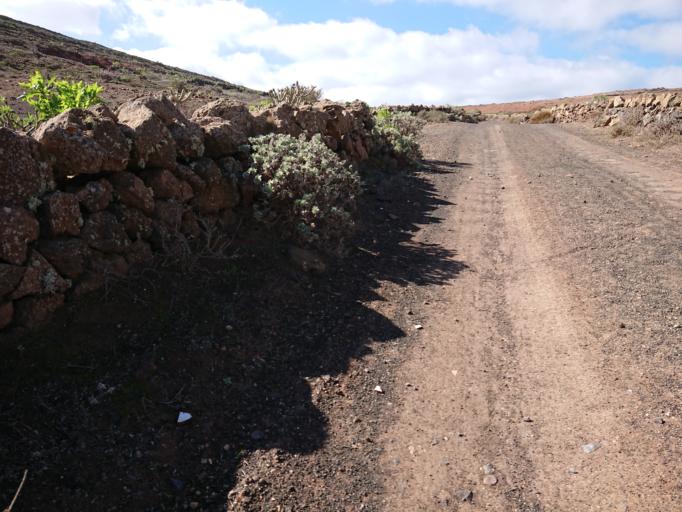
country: ES
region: Canary Islands
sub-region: Provincia de Las Palmas
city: Haria
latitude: 29.1456
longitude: -13.5165
